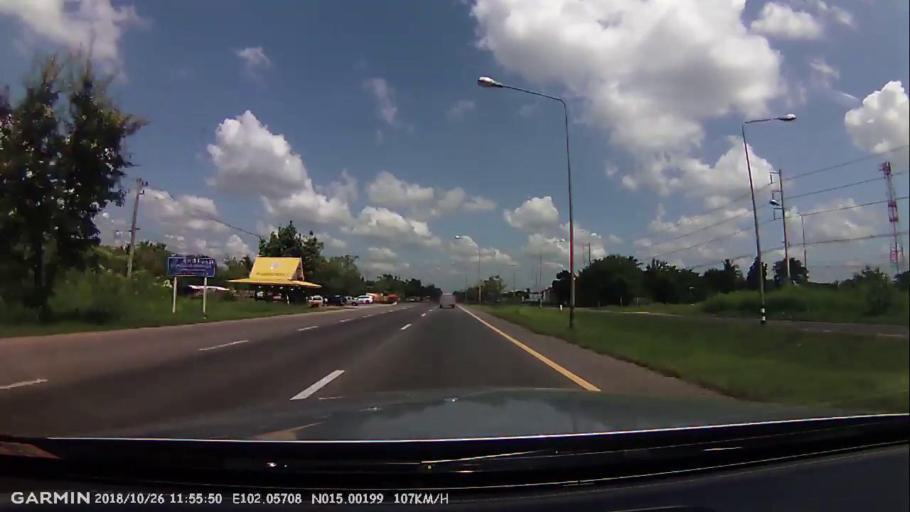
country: TH
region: Nakhon Ratchasima
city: Nakhon Ratchasima
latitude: 15.0022
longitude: 102.0572
